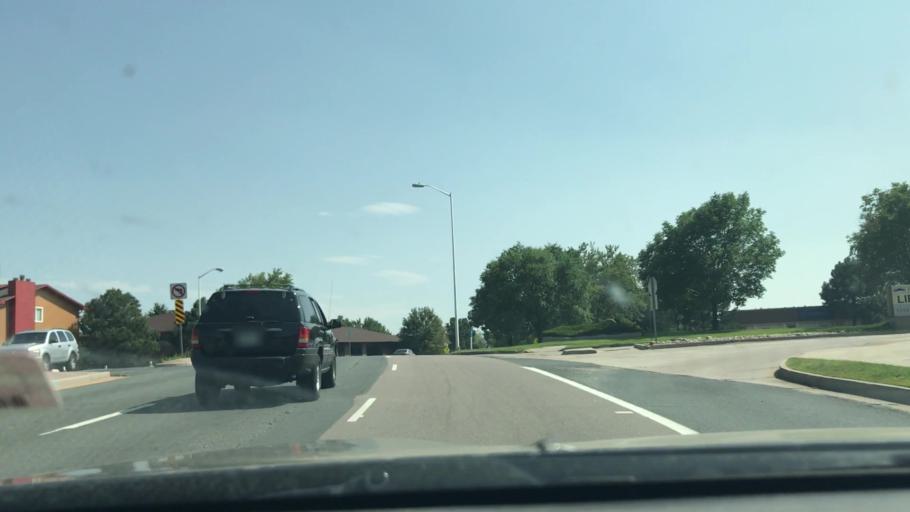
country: US
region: Colorado
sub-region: El Paso County
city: Colorado Springs
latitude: 38.9130
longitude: -104.7753
